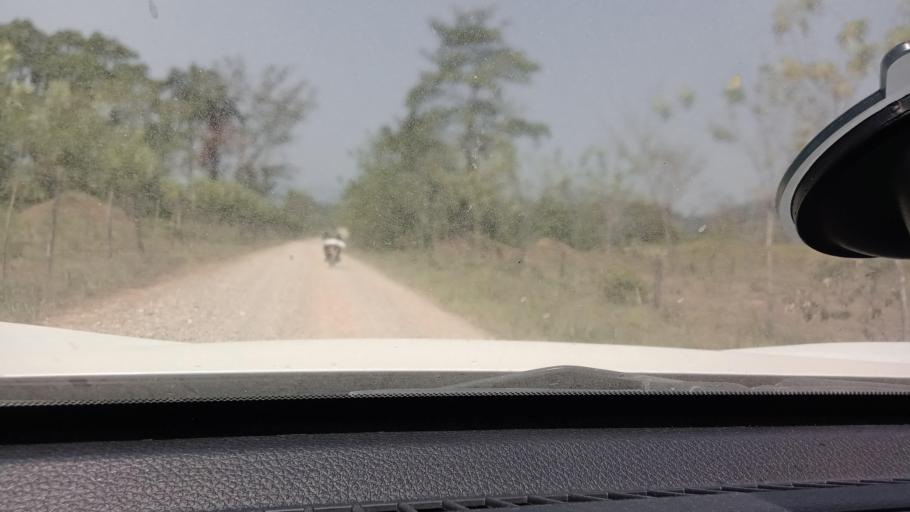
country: MX
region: Tabasco
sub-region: Huimanguillo
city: Francisco Rueda
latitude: 17.5152
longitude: -93.8929
